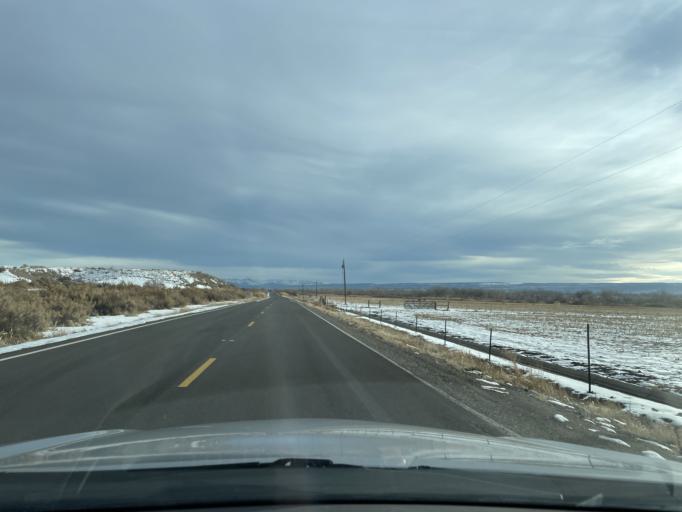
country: US
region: Colorado
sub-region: Montrose County
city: Olathe
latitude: 38.6561
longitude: -107.9971
